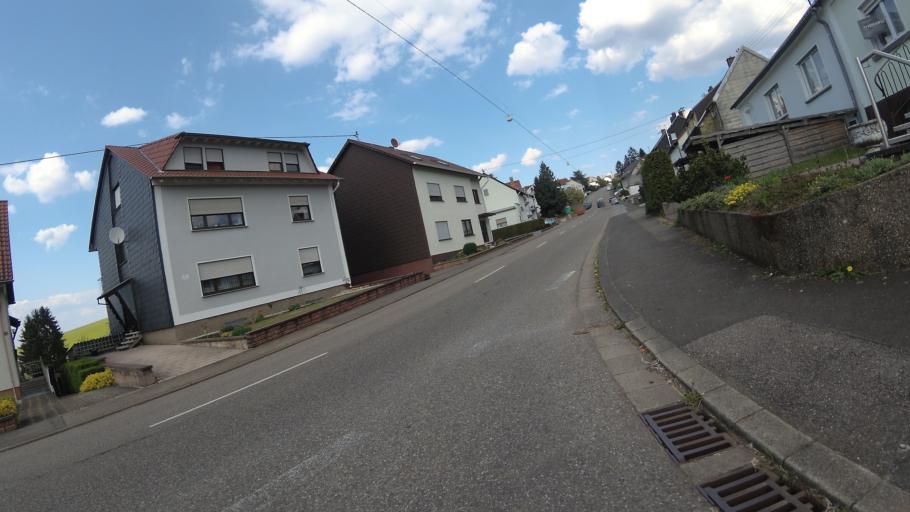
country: DE
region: Saarland
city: Riegelsberg
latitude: 49.2956
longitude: 6.9234
